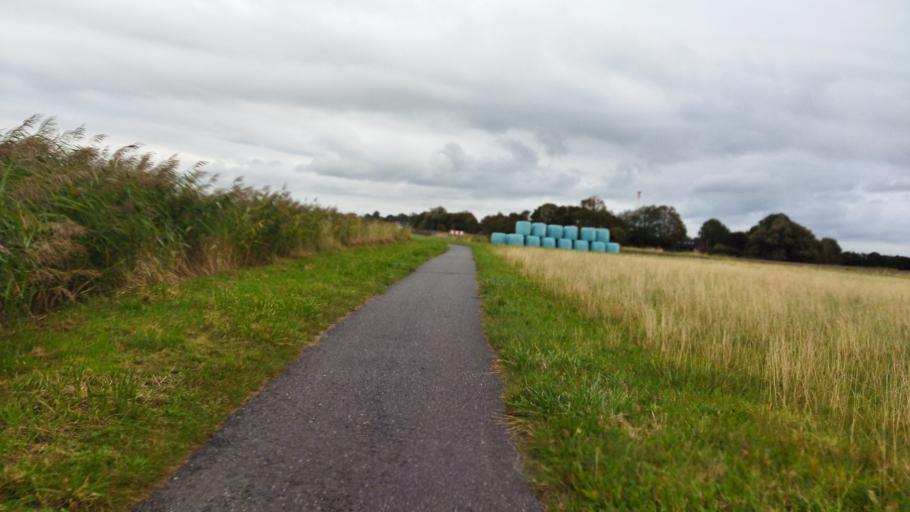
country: DE
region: Lower Saxony
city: Wirdum
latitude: 53.4932
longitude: 7.1121
